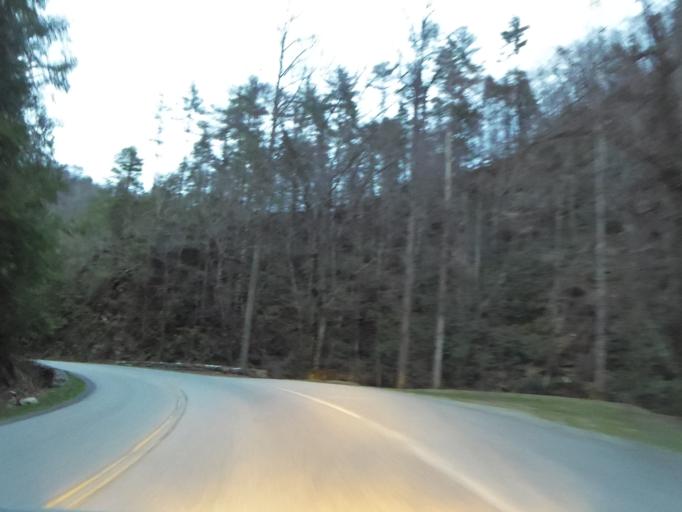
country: US
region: Tennessee
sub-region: Sevier County
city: Gatlinburg
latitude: 35.6393
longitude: -83.7171
